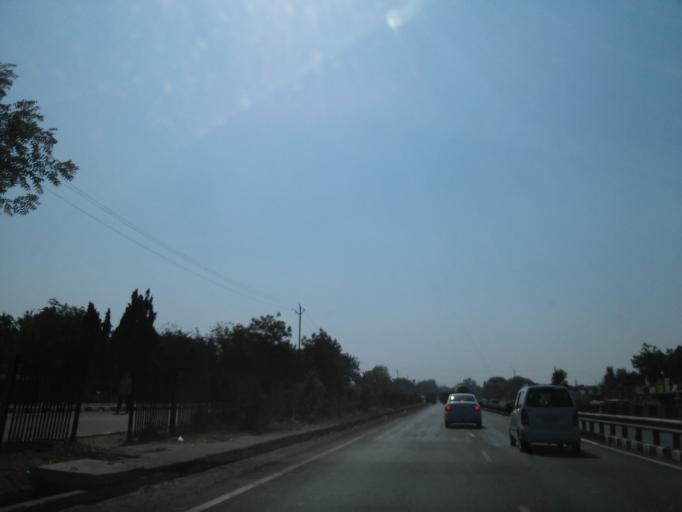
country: IN
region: Gujarat
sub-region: Gandhinagar
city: Ghandinagar
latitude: 23.2316
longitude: 72.7332
